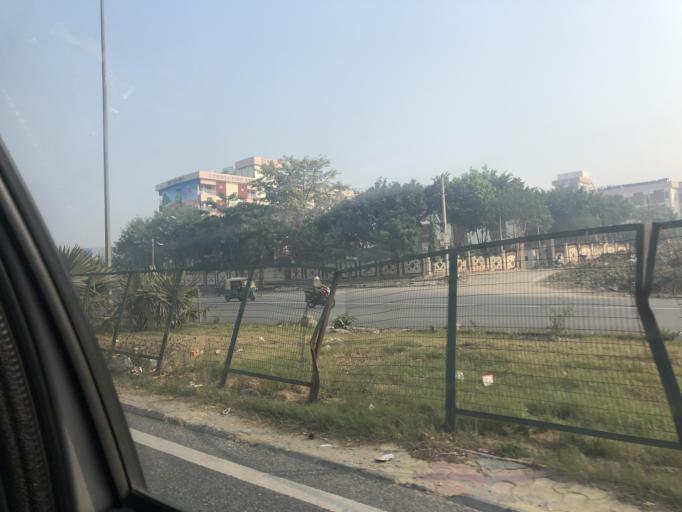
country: IN
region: NCT
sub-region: Central Delhi
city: Karol Bagh
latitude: 28.6144
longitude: 77.1364
